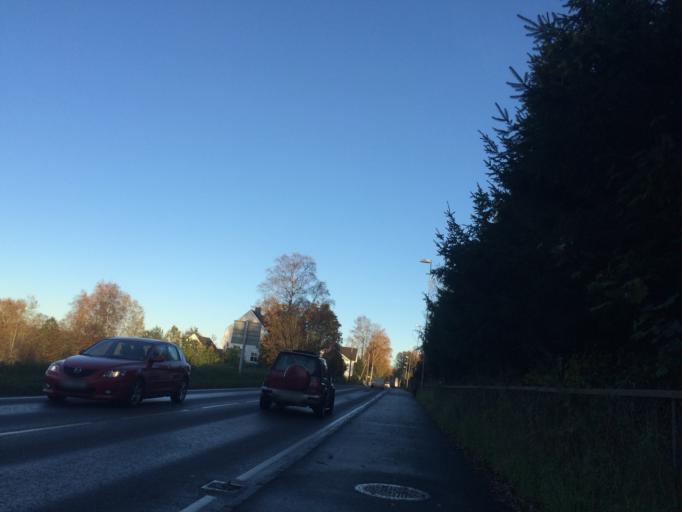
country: NO
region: Akershus
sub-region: Ski
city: Ski
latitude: 59.7215
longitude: 10.8492
